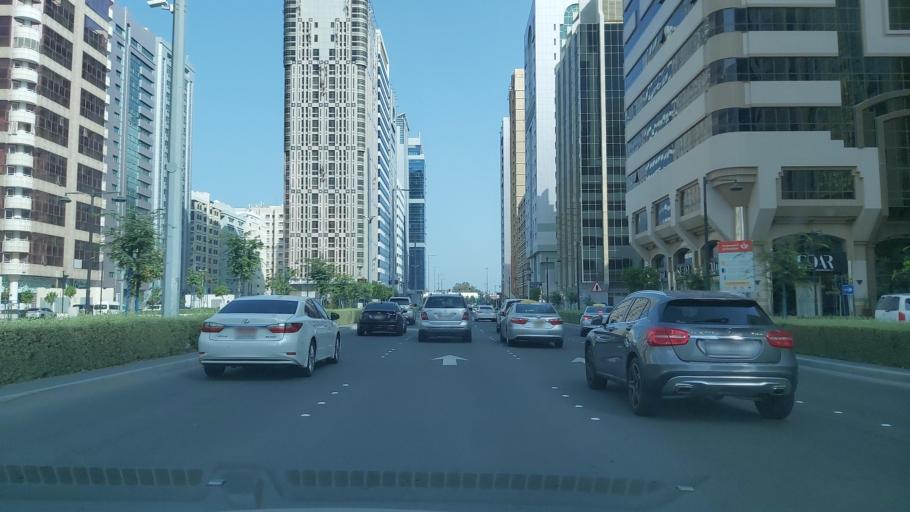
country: AE
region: Abu Dhabi
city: Abu Dhabi
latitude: 24.5018
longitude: 54.3771
